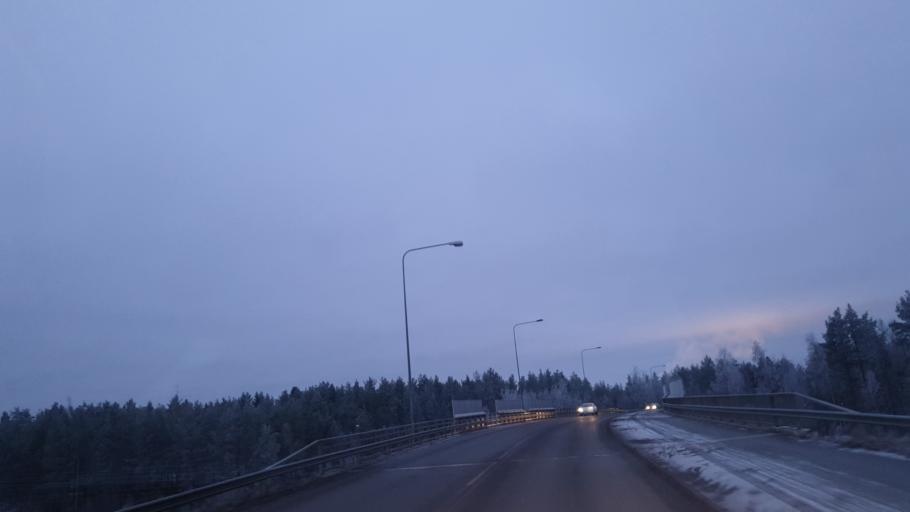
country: FI
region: Southern Ostrobothnia
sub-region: Seinaejoki
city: Nurmo
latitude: 62.7744
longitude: 22.8887
